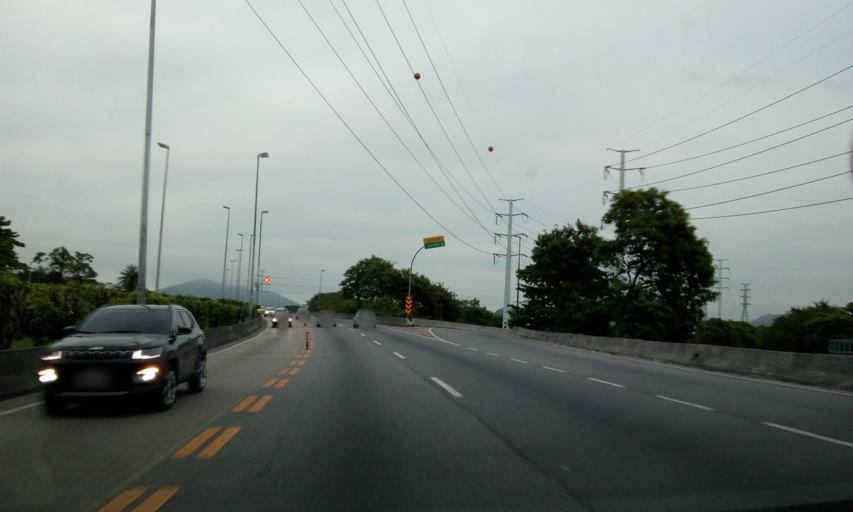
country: BR
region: Rio de Janeiro
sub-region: Rio De Janeiro
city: Rio de Janeiro
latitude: -22.8717
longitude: -43.2650
